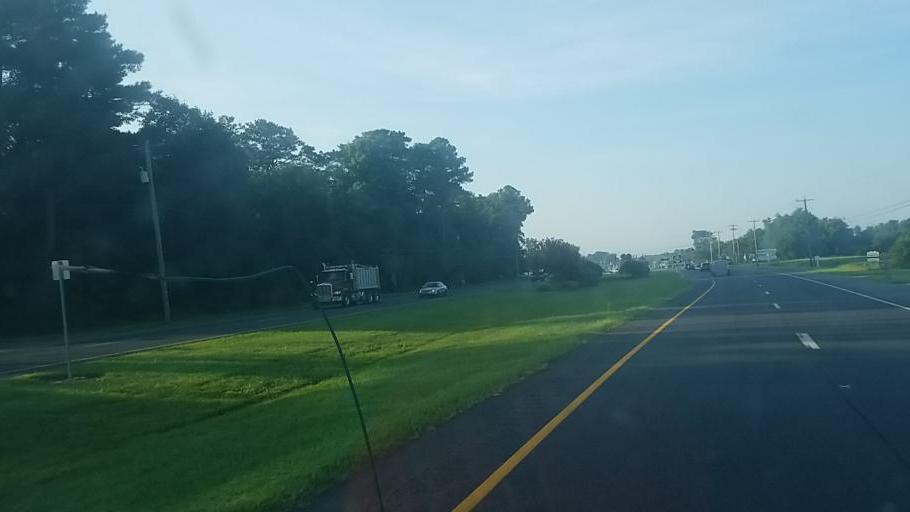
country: US
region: Delaware
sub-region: Sussex County
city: Selbyville
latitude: 38.4656
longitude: -75.2342
